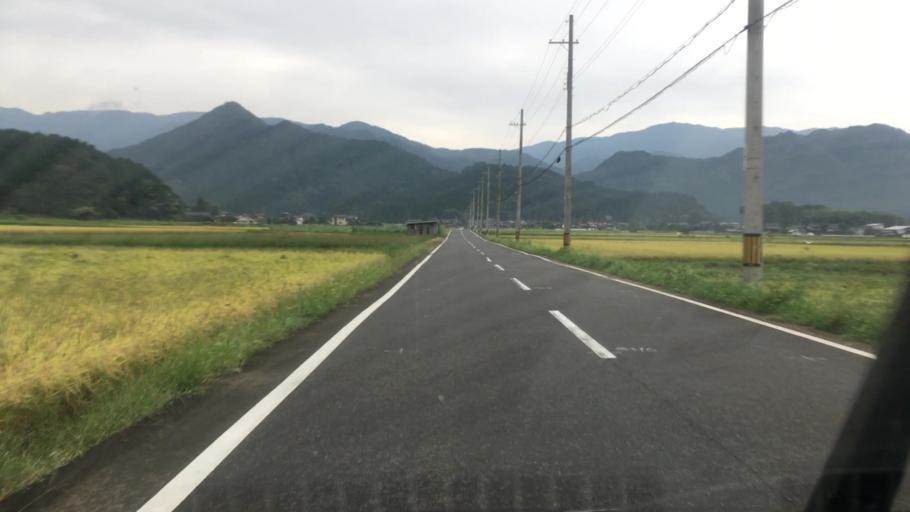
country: JP
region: Hyogo
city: Toyooka
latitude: 35.4517
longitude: 134.7336
